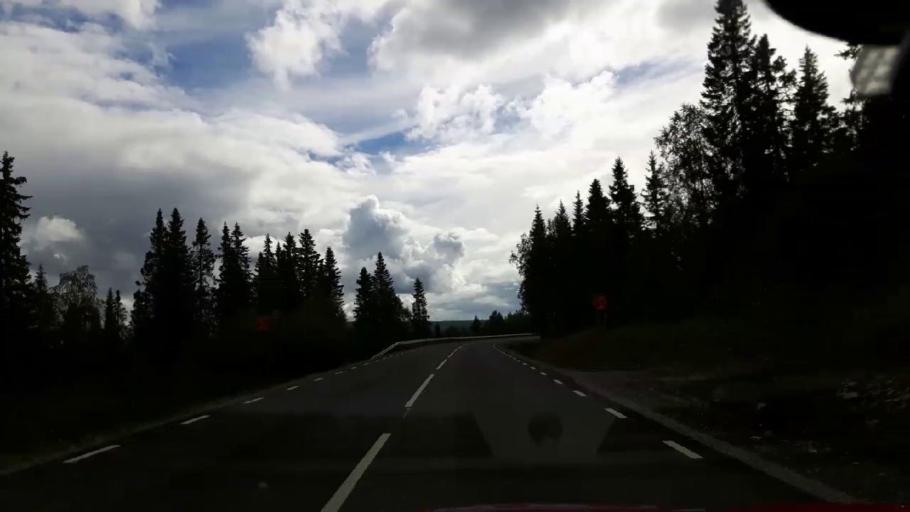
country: NO
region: Nord-Trondelag
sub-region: Royrvik
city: Royrvik
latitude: 64.8068
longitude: 14.0707
